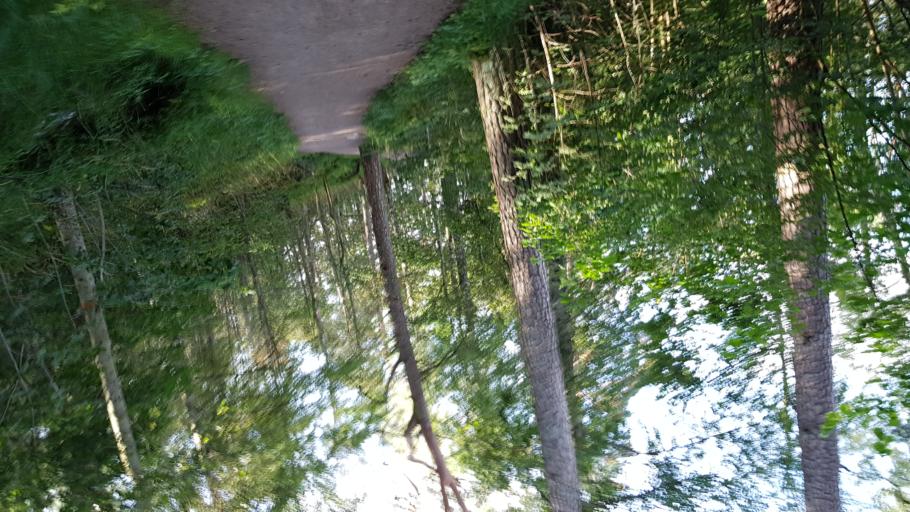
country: SE
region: Vaestra Goetaland
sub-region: Molndal
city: Moelndal
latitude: 57.6877
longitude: 12.0337
